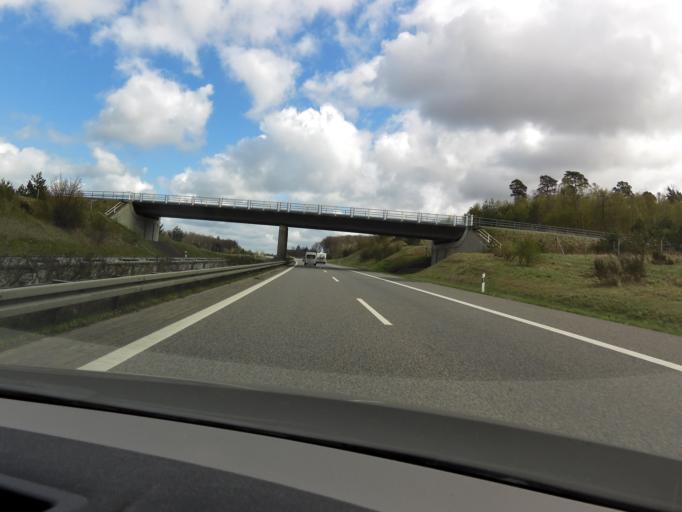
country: DE
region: Mecklenburg-Vorpommern
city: Tessin
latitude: 54.0103
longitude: 12.4672
